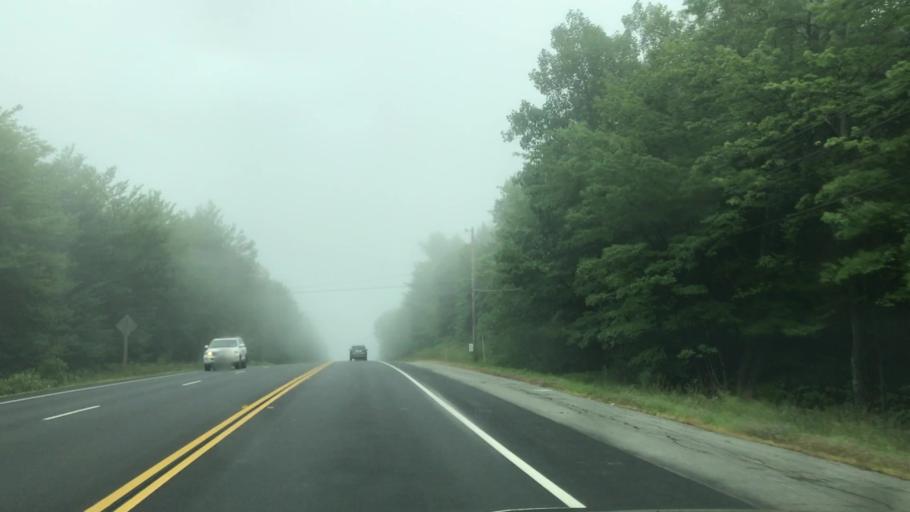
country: US
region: Maine
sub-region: Lincoln County
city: Waldoboro
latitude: 44.1081
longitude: -69.3428
